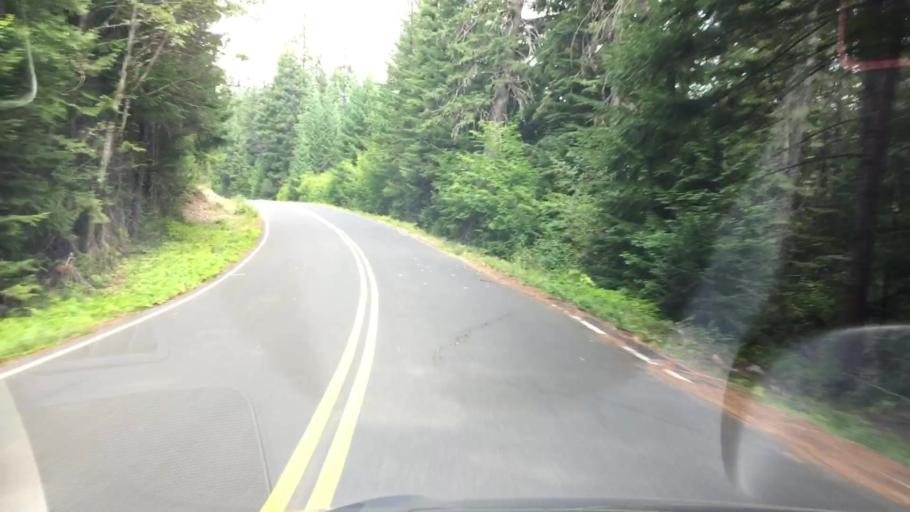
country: US
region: Washington
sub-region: Klickitat County
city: White Salmon
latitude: 46.0973
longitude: -121.6086
